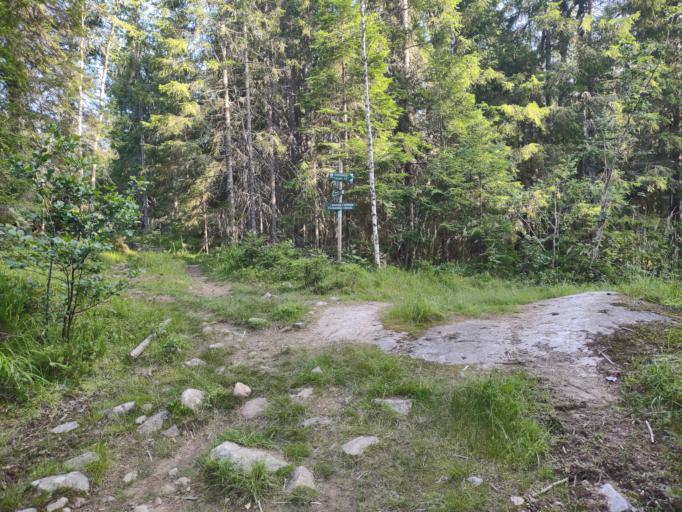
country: NO
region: Akershus
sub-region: Lorenskog
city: Kjenn
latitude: 59.8442
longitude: 11.0053
